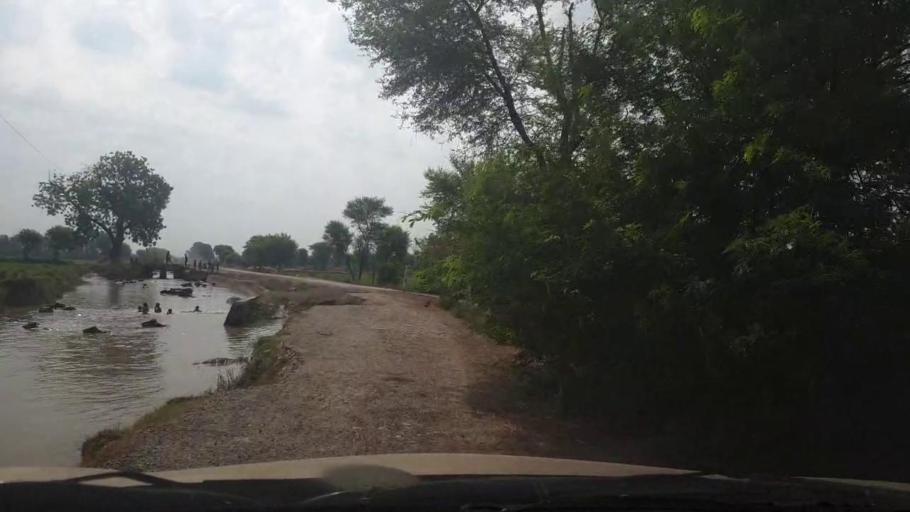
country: PK
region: Sindh
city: Larkana
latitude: 27.6379
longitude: 68.2072
